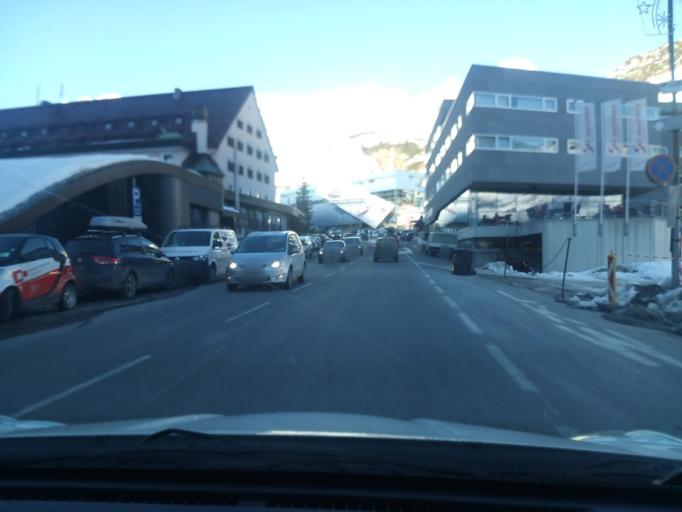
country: AT
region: Tyrol
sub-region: Politischer Bezirk Landeck
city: Sankt Anton am Arlberg
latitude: 47.1255
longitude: 10.2144
